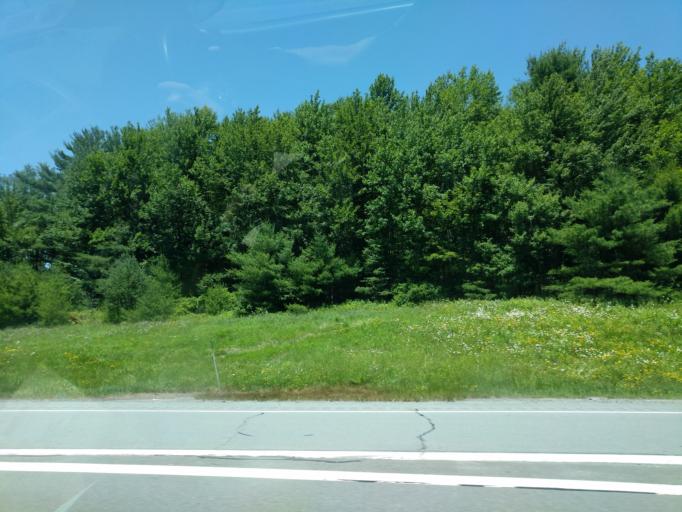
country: US
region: New York
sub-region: Sullivan County
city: Rock Hill
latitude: 41.6392
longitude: -74.6297
